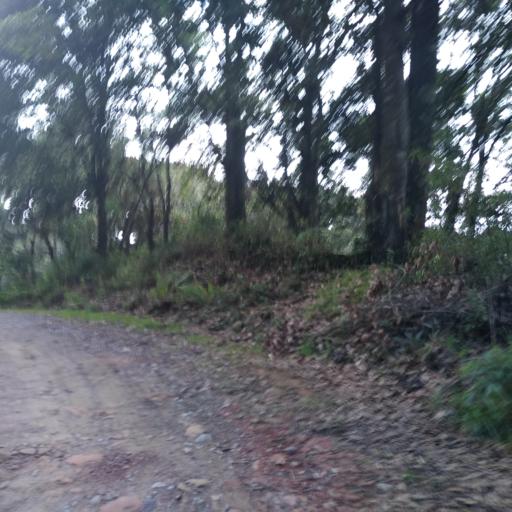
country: CO
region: Boyaca
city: Duitama
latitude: 5.9470
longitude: -73.1443
